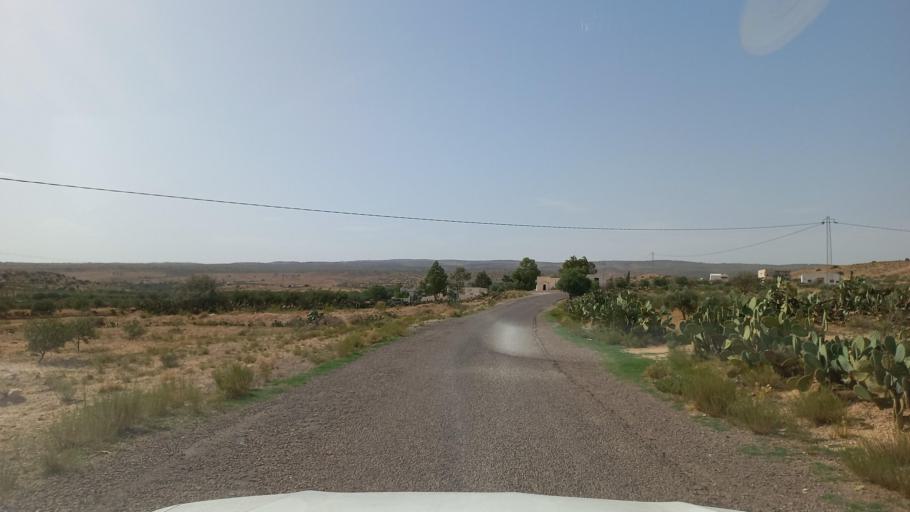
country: TN
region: Al Qasrayn
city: Kasserine
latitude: 35.3006
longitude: 8.9516
